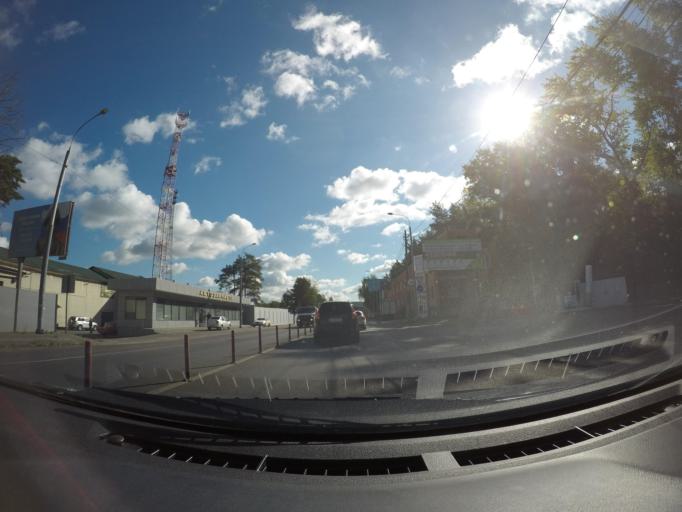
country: RU
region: Moskovskaya
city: Korenevo
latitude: 55.6630
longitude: 38.0034
